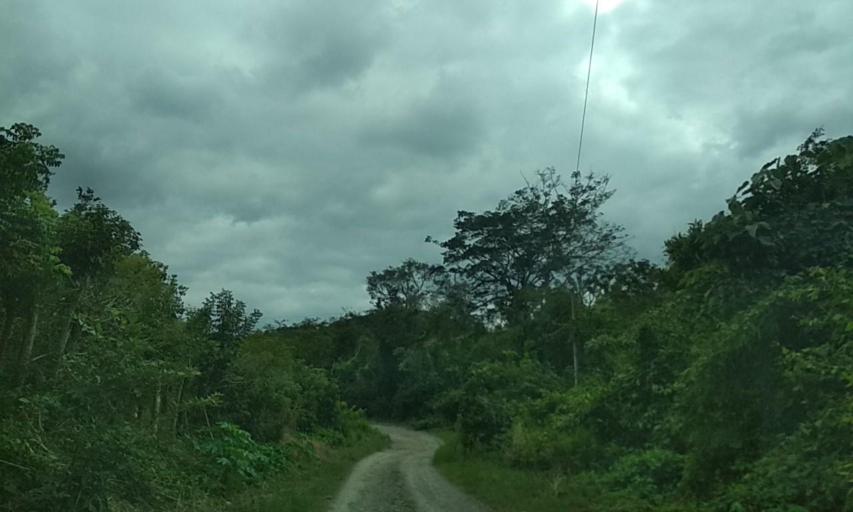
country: MX
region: Veracruz
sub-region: Papantla
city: Polutla
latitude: 20.5281
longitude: -97.2985
